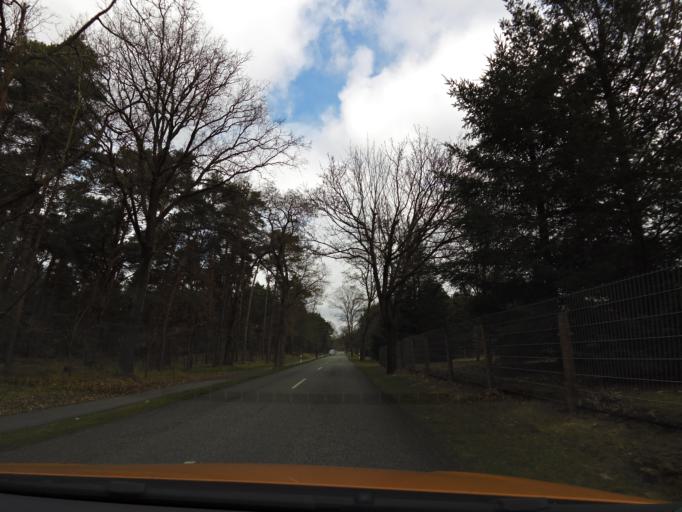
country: DE
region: Brandenburg
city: Rathenow
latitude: 52.6377
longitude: 12.3652
